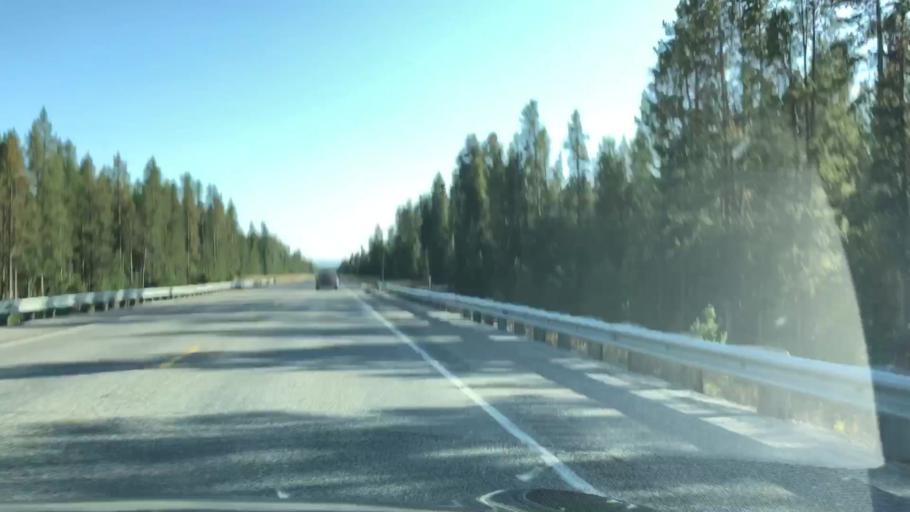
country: US
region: Montana
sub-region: Gallatin County
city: West Yellowstone
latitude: 44.7539
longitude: -111.1133
